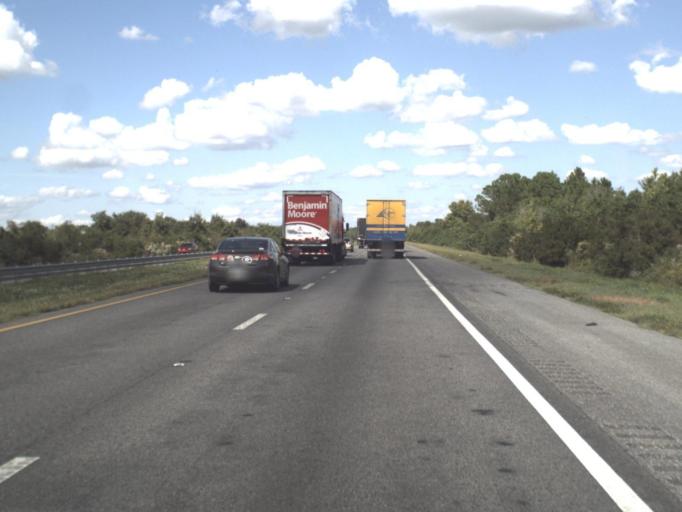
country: US
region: Florida
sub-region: Brevard County
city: June Park
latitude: 27.8319
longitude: -81.0049
